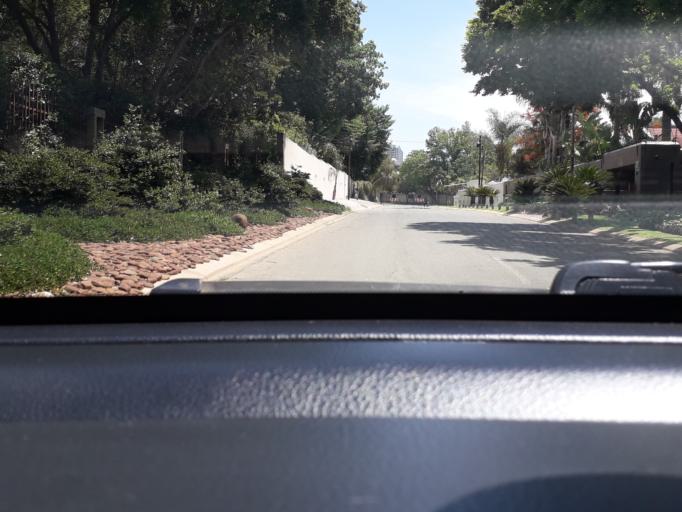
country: ZA
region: Gauteng
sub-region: City of Johannesburg Metropolitan Municipality
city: Modderfontein
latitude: -26.0976
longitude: 28.0722
